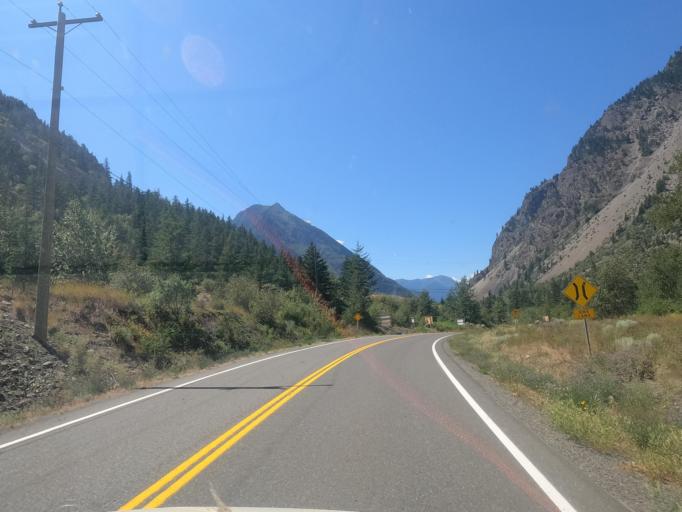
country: CA
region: British Columbia
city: Lillooet
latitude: 50.6700
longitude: -121.9677
